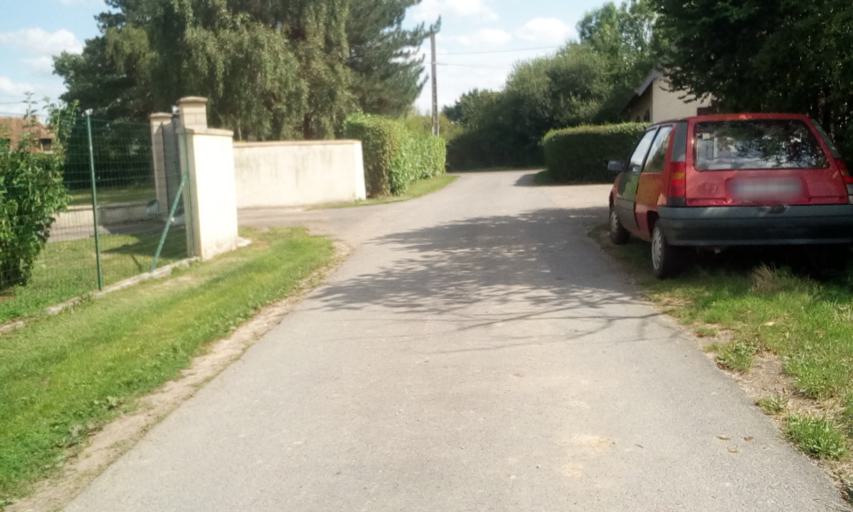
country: FR
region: Lower Normandy
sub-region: Departement du Calvados
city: Argences
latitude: 49.1448
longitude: -0.1484
